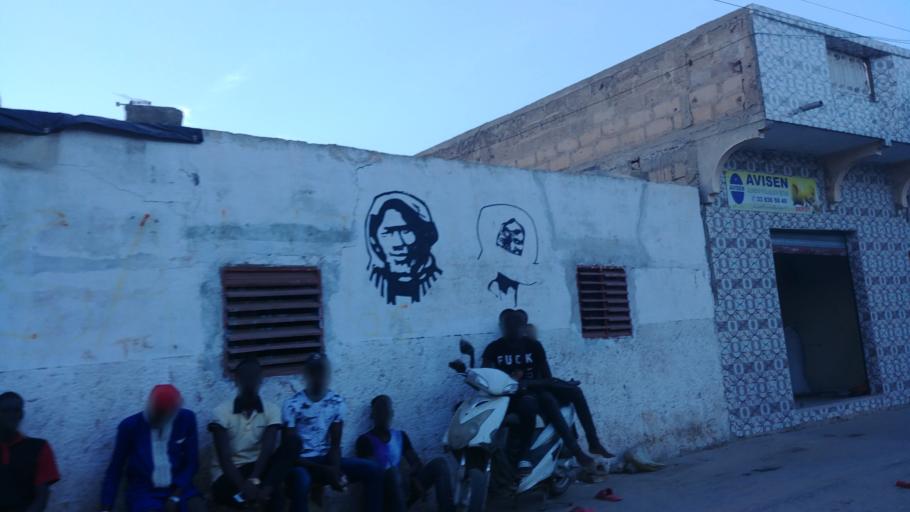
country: SN
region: Saint-Louis
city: Saint-Louis
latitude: 16.0103
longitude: -16.4889
